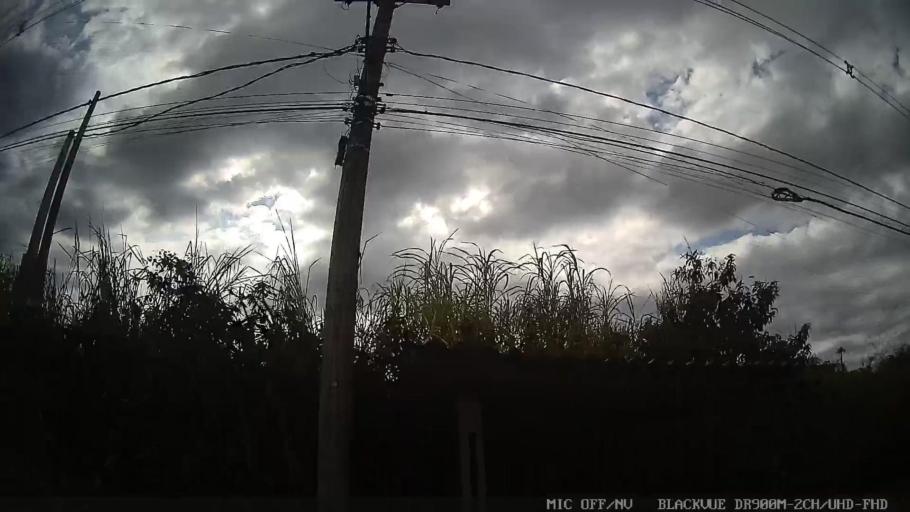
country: BR
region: Sao Paulo
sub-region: Indaiatuba
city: Indaiatuba
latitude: -23.1525
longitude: -47.1486
